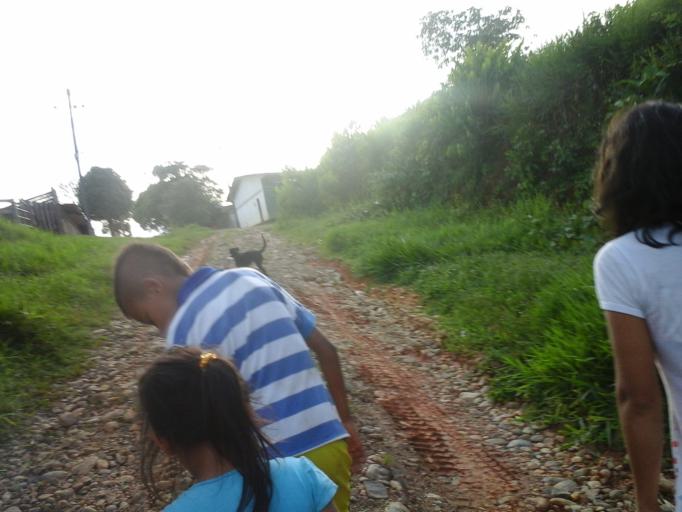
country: CO
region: Caqueta
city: El Doncello
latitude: 1.6110
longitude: -74.9940
